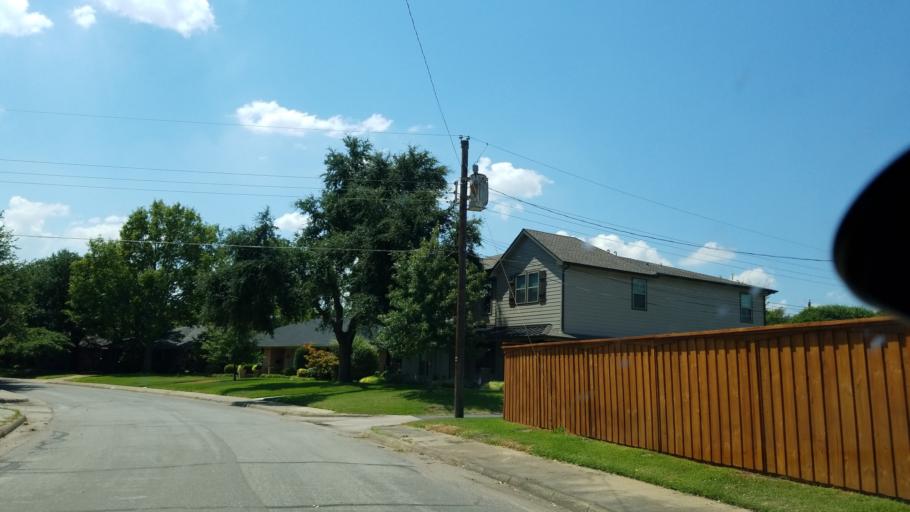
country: US
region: Texas
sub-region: Dallas County
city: Richardson
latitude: 32.8919
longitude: -96.7117
